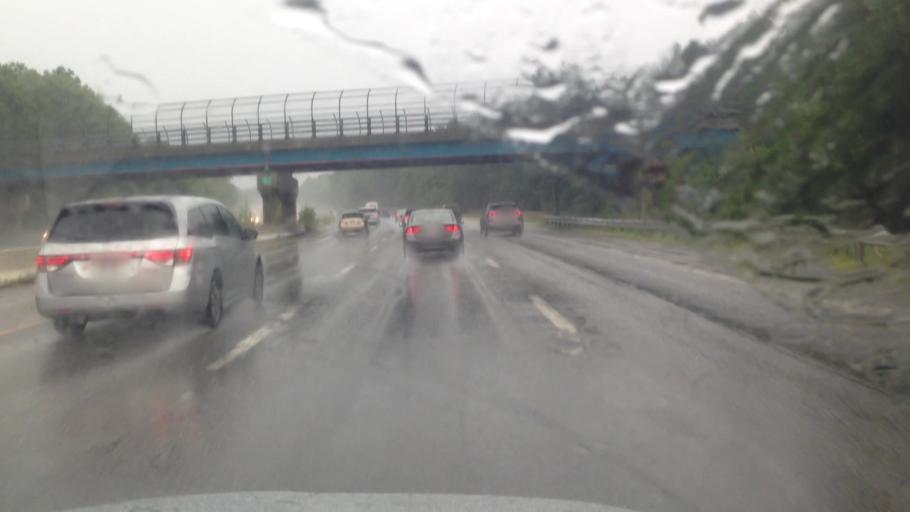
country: US
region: Massachusetts
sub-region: Middlesex County
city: Cochituate
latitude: 42.3194
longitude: -71.3431
